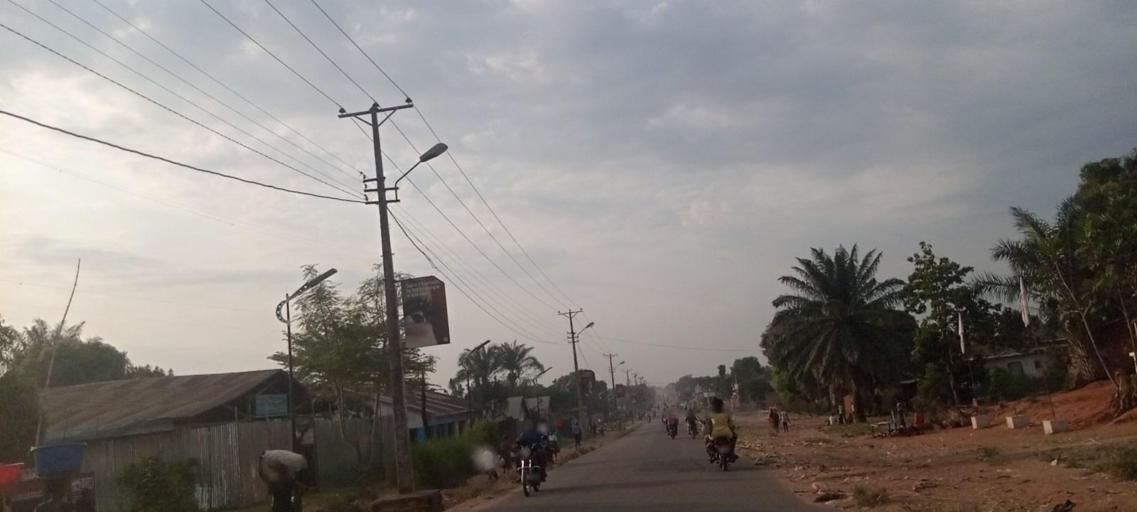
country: CD
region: Kasai-Oriental
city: Mbuji-Mayi
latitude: -6.1266
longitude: 23.6003
